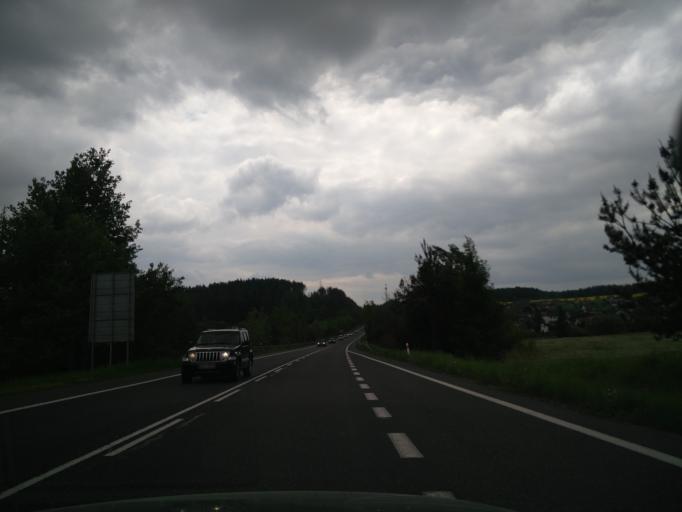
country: CZ
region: Central Bohemia
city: Milin
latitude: 49.6343
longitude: 14.0515
